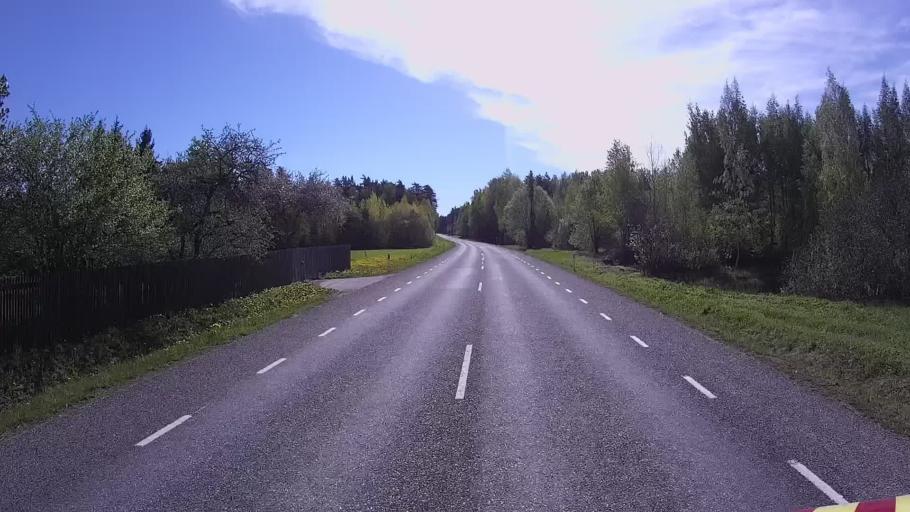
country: EE
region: Polvamaa
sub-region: Raepina vald
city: Rapina
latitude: 58.0992
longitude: 27.3874
